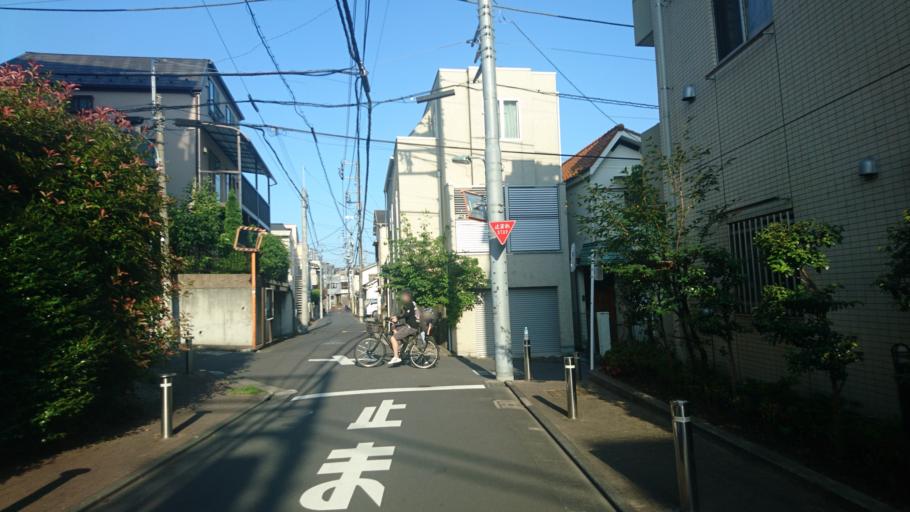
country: JP
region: Tokyo
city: Tokyo
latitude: 35.6148
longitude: 139.7216
